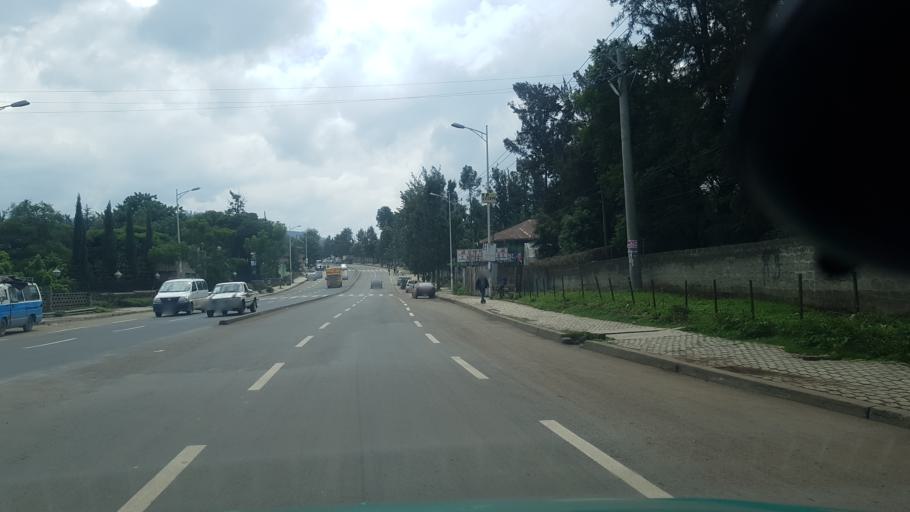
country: ET
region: Adis Abeba
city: Addis Ababa
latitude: 9.0206
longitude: 38.7715
